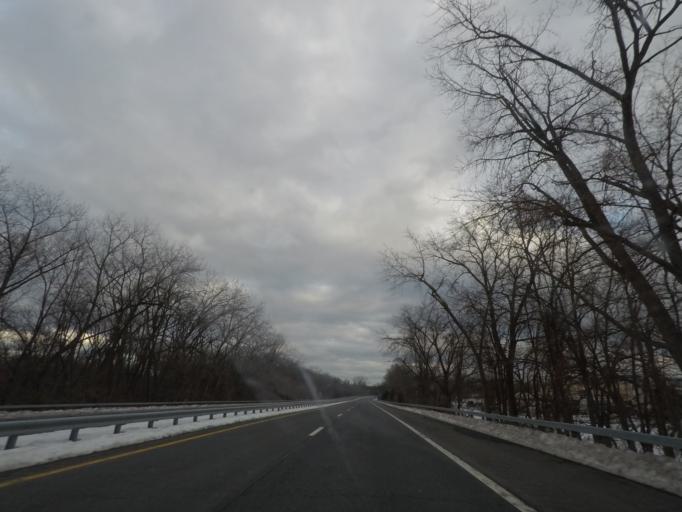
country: US
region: New York
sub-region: Ulster County
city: Kingston
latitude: 41.9385
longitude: -74.0171
